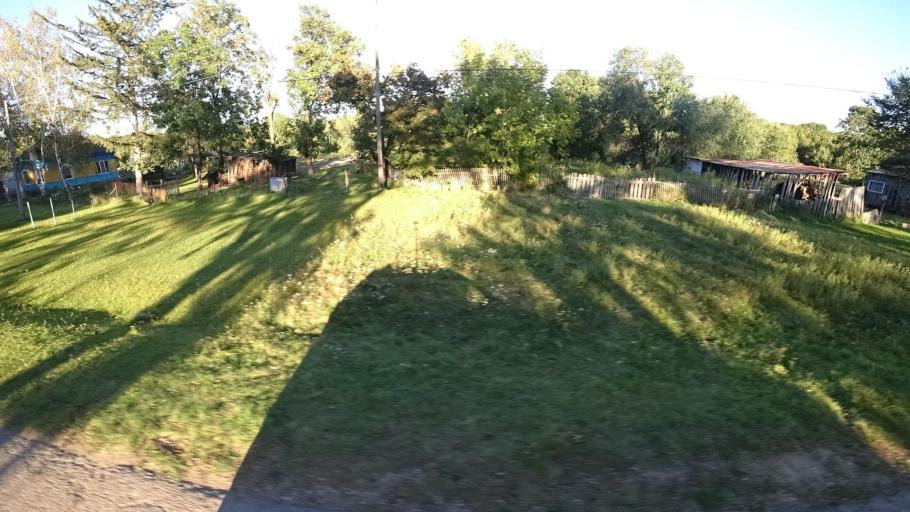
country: RU
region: Primorskiy
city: Kirovskiy
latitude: 44.8283
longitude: 133.5751
